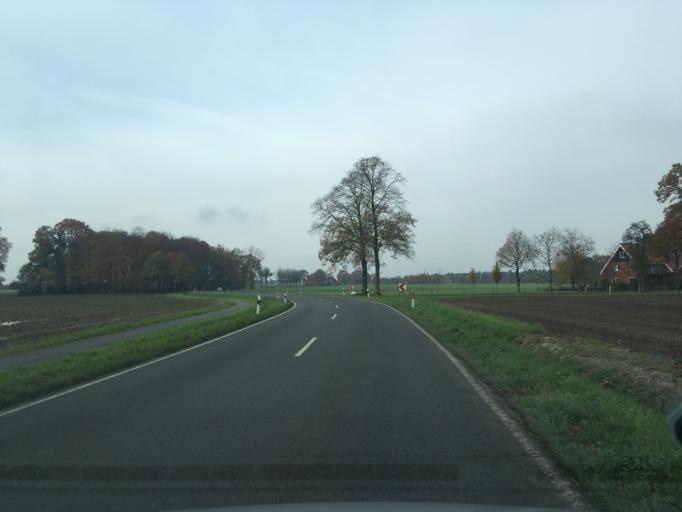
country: DE
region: North Rhine-Westphalia
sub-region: Regierungsbezirk Munster
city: Velen
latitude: 51.9115
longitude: 6.9680
